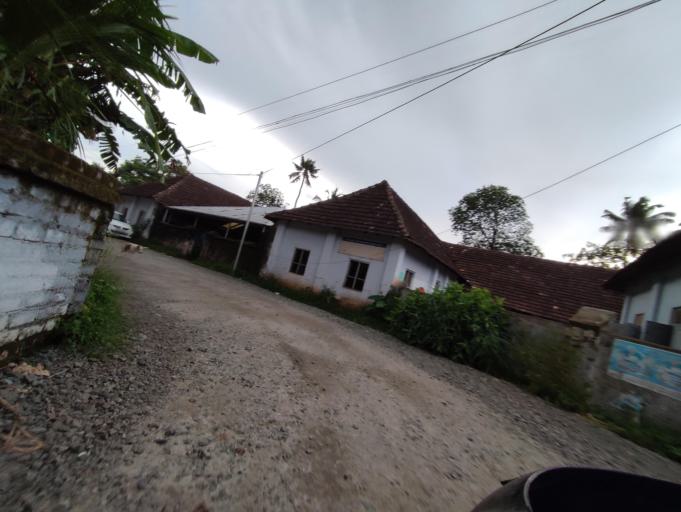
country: IN
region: Kerala
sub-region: Alappuzha
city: Vayalar
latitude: 9.6894
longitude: 76.3362
